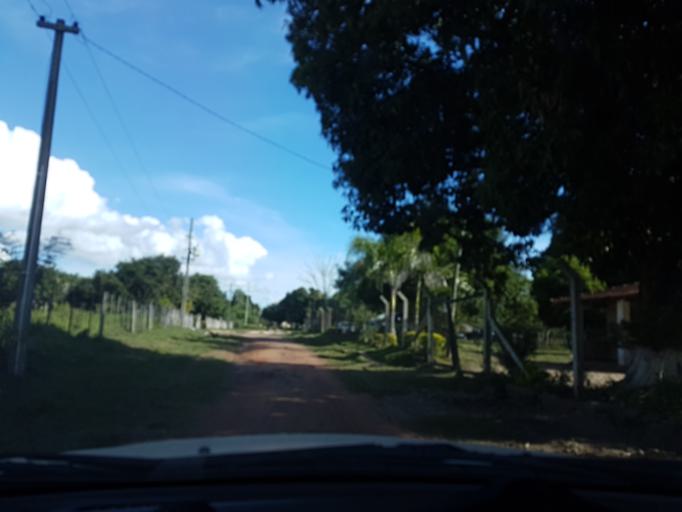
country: PY
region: Cordillera
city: Arroyos y Esteros
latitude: -24.9791
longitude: -57.1958
